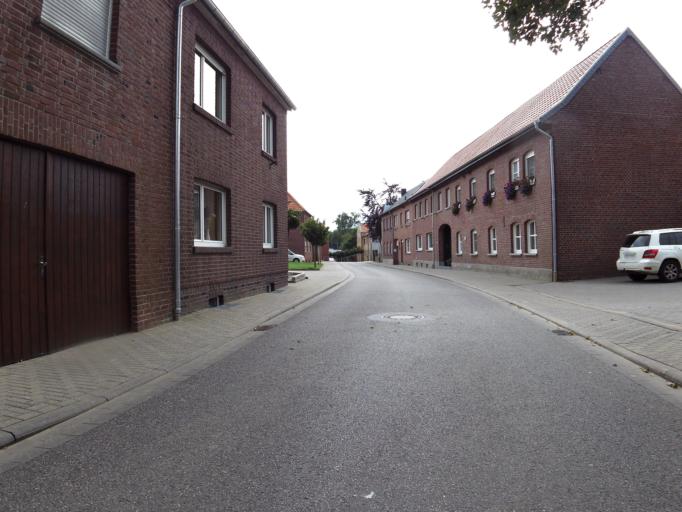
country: DE
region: North Rhine-Westphalia
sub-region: Regierungsbezirk Koln
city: Gangelt
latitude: 51.0192
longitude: 6.0389
